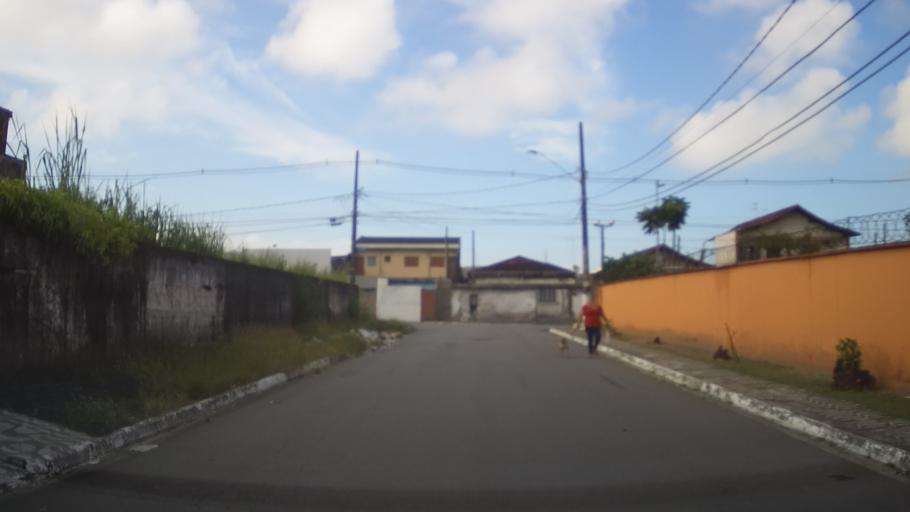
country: BR
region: Sao Paulo
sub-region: Praia Grande
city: Praia Grande
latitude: -24.0164
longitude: -46.4792
